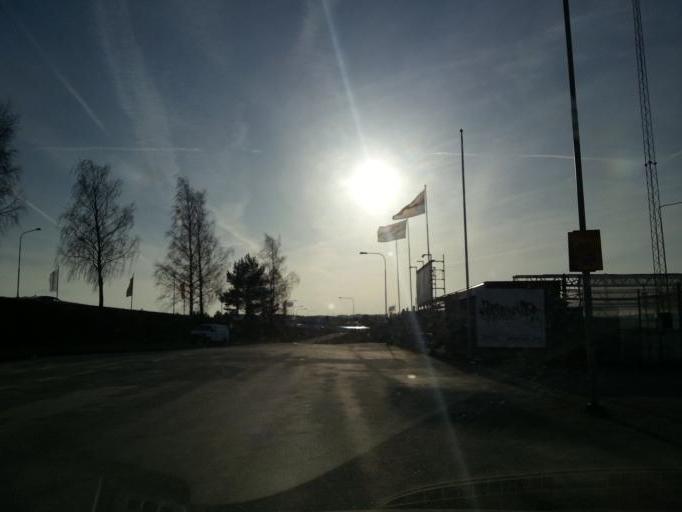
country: SE
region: Joenkoeping
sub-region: Jonkopings Kommun
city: Jonkoping
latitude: 57.7650
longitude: 14.1670
